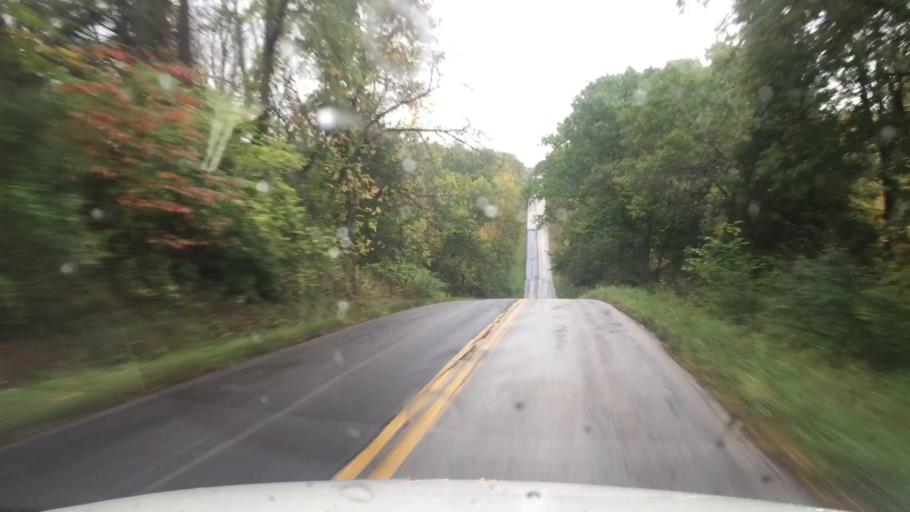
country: US
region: Missouri
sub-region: Boone County
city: Columbia
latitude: 38.9367
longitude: -92.4965
